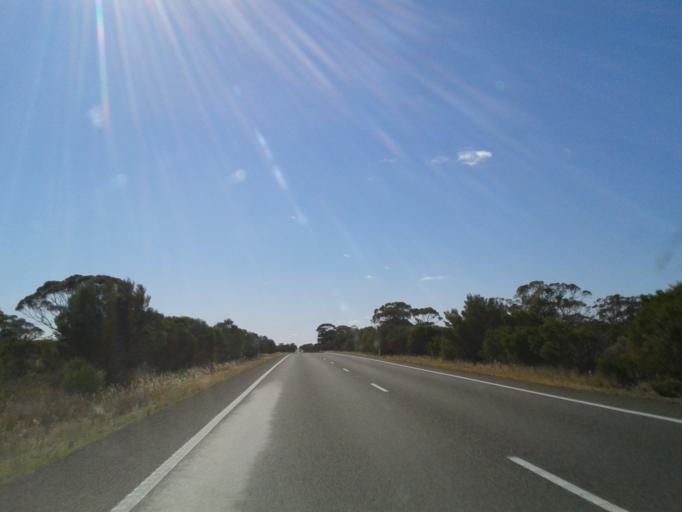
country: AU
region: South Australia
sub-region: Renmark Paringa
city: Renmark
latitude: -34.2743
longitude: 140.9789
